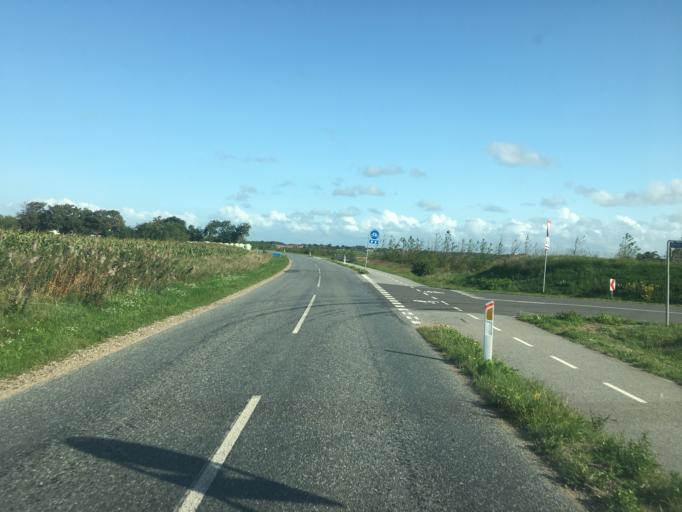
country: DK
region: South Denmark
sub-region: Tonder Kommune
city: Sherrebek
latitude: 55.1387
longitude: 8.7615
